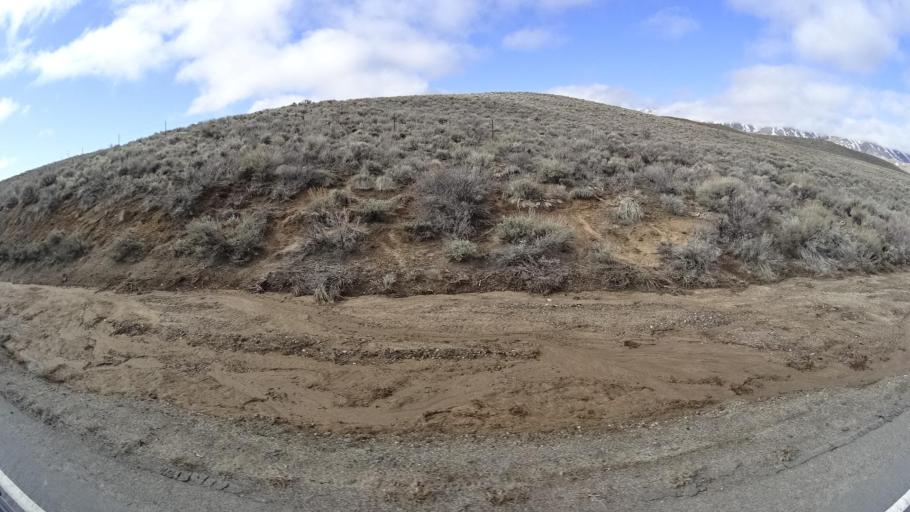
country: US
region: Nevada
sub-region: Washoe County
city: Cold Springs
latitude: 39.7995
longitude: -119.9029
